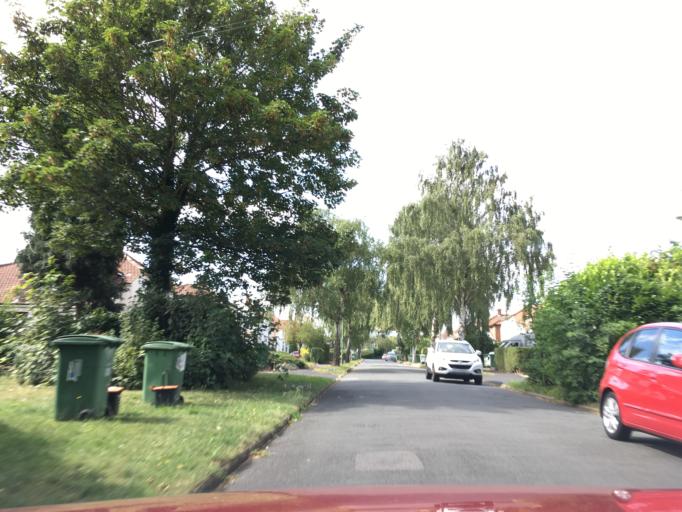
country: GB
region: England
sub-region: Kent
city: Maidstone
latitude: 51.2831
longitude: 0.5051
